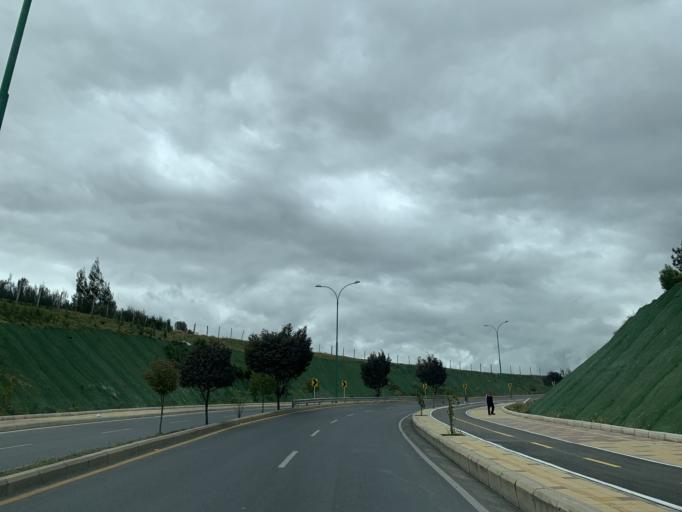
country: CO
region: Boyaca
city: Tunja
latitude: 5.5370
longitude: -73.3463
